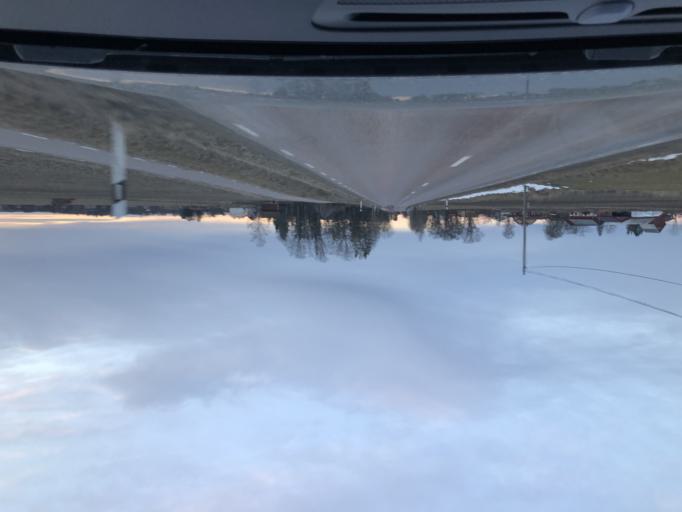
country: SE
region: Uppsala
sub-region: Uppsala Kommun
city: Gamla Uppsala
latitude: 59.9173
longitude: 17.6424
